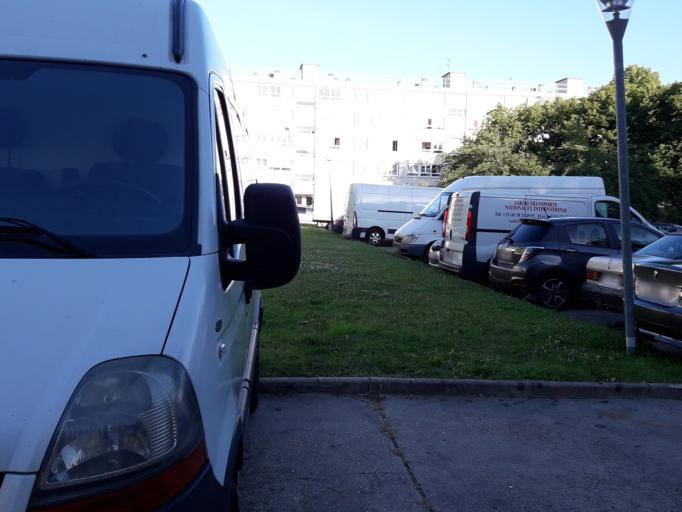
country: FR
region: Ile-de-France
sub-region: Departement de l'Essonne
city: Sainte-Genevieve-des-Bois
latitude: 48.6340
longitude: 2.3254
